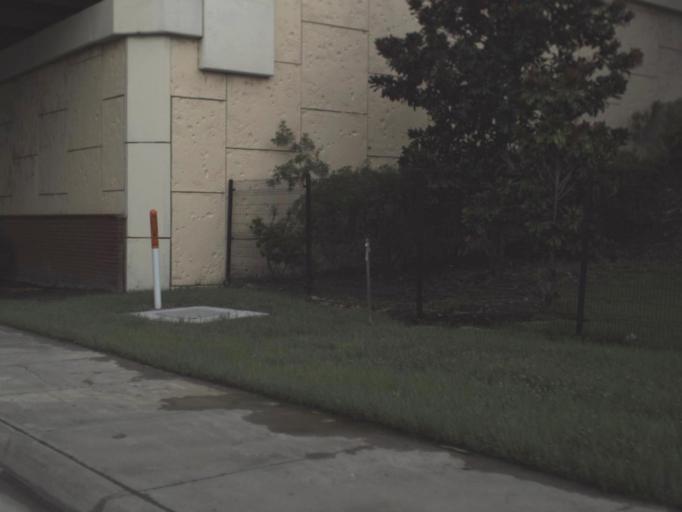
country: US
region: Florida
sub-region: Hillsborough County
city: East Lake-Orient Park
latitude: 27.9652
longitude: -82.4140
